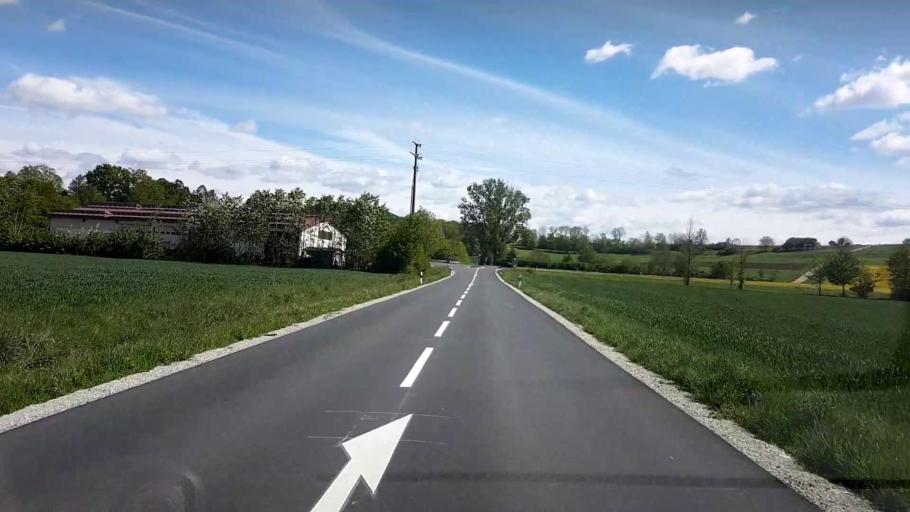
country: DE
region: Bavaria
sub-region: Upper Franconia
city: Buttenheim
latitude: 49.8042
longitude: 11.0421
